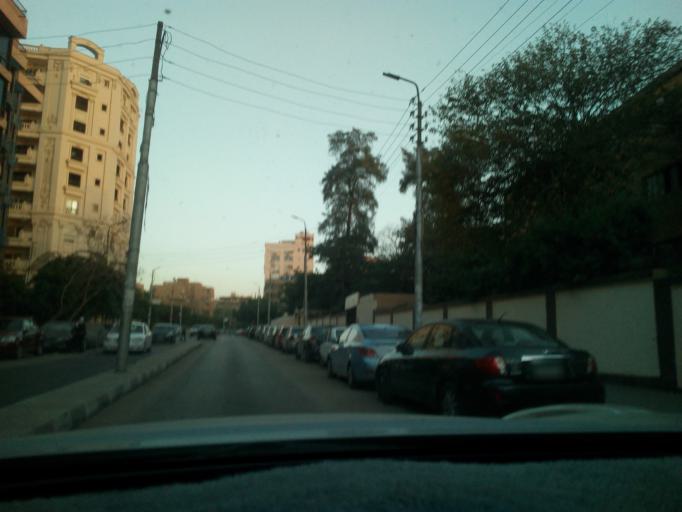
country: EG
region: Muhafazat al Qahirah
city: Cairo
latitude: 30.0907
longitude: 31.3441
